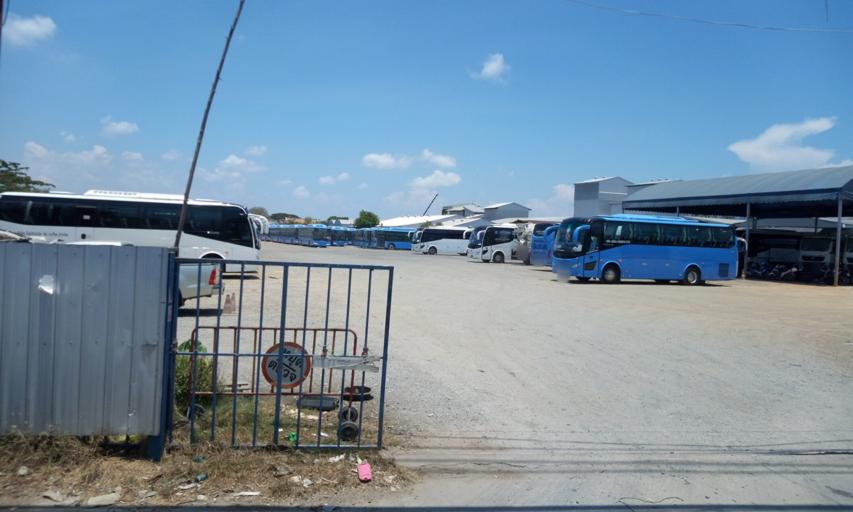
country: TH
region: Bangkok
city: Bang Na
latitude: 13.6260
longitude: 100.7066
